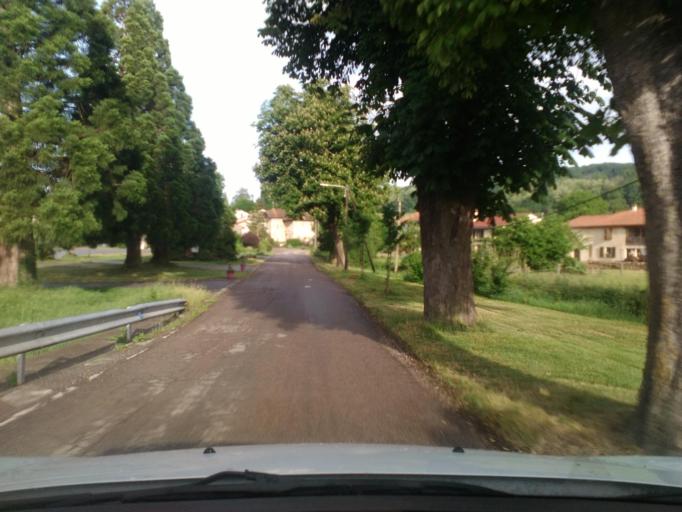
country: FR
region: Lorraine
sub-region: Departement de Meurthe-et-Moselle
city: Gerbeviller
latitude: 48.4637
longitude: 6.5518
